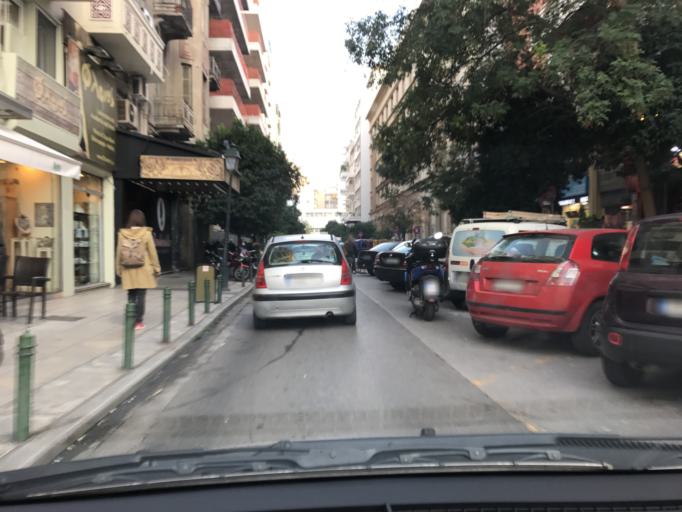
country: GR
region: Central Macedonia
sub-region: Nomos Thessalonikis
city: Thessaloniki
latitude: 40.6340
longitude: 22.9428
